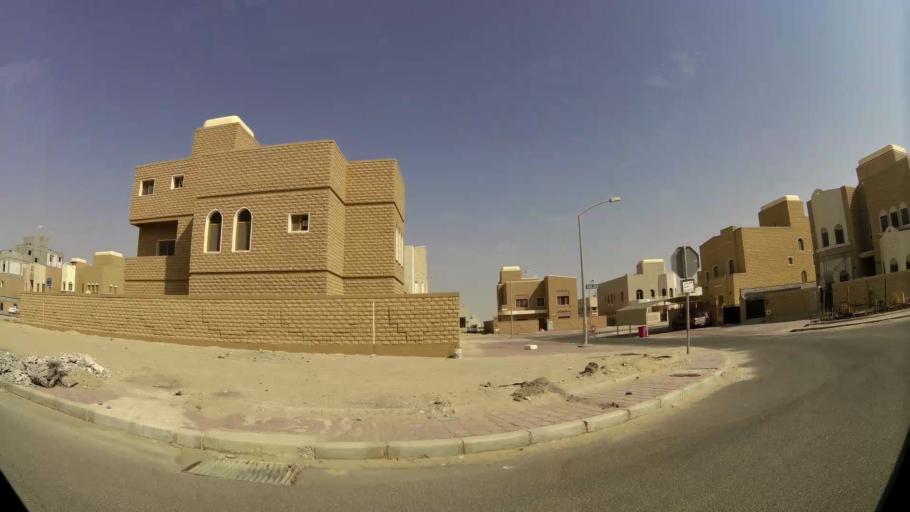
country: KW
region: Al Ahmadi
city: Al Wafrah
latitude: 28.8042
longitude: 48.0589
